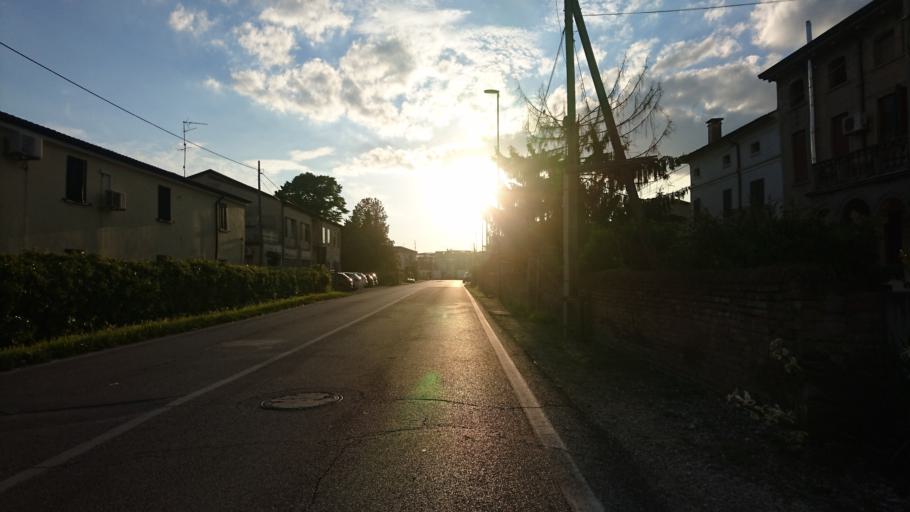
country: IT
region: Veneto
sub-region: Provincia di Rovigo
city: Castelmassa
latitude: 45.0217
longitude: 11.3187
